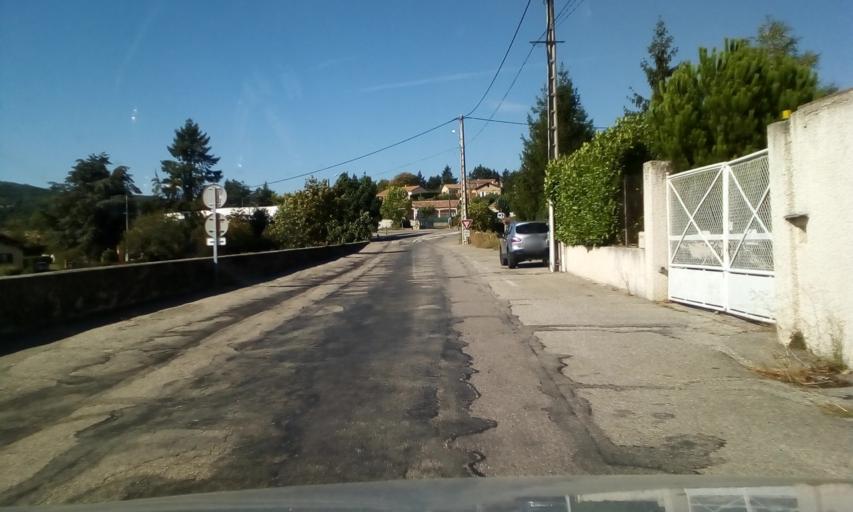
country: FR
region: Rhone-Alpes
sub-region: Departement de l'Ardeche
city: Boulieu-les-Annonay
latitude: 45.2625
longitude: 4.6658
